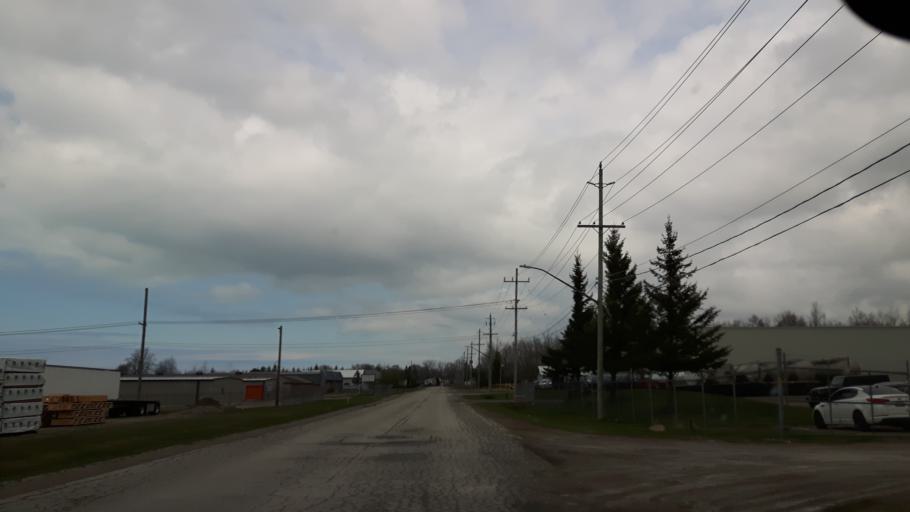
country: CA
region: Ontario
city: Goderich
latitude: 43.7273
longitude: -81.6994
